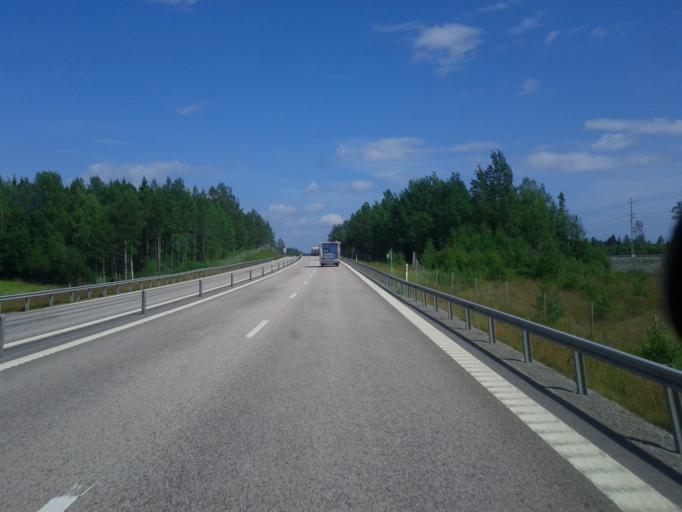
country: SE
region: Vaesterbotten
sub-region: Nordmalings Kommun
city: Nordmaling
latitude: 63.5050
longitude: 19.3461
